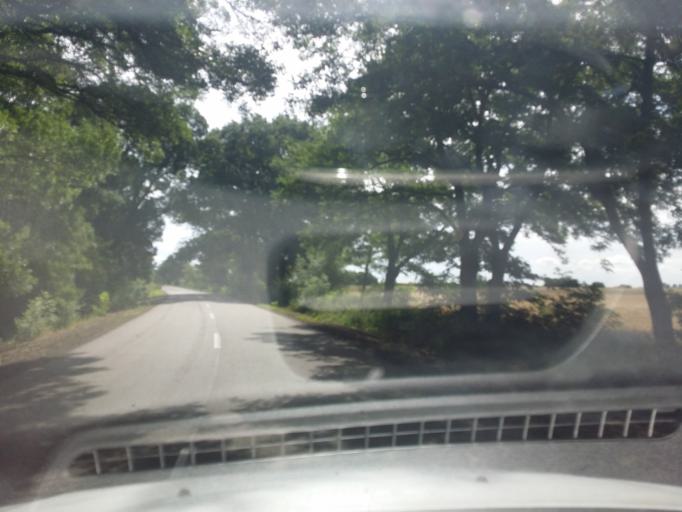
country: HU
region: Heves
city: Besenyotelek
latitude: 47.6032
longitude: 20.4146
